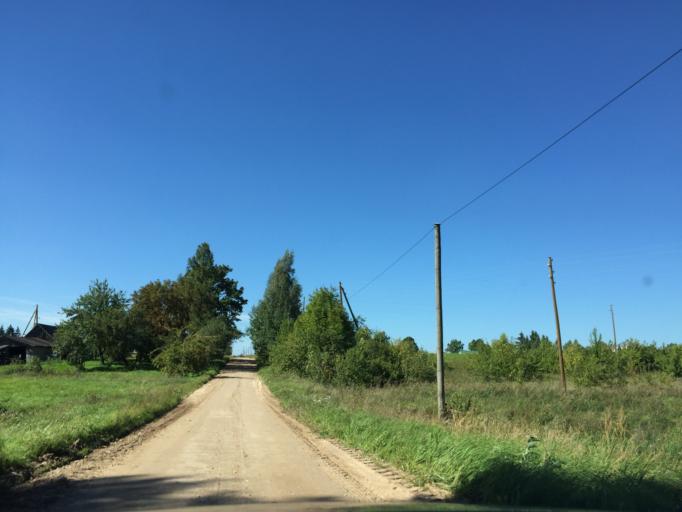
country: LV
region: Akniste
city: Akniste
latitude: 56.1587
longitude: 25.7391
